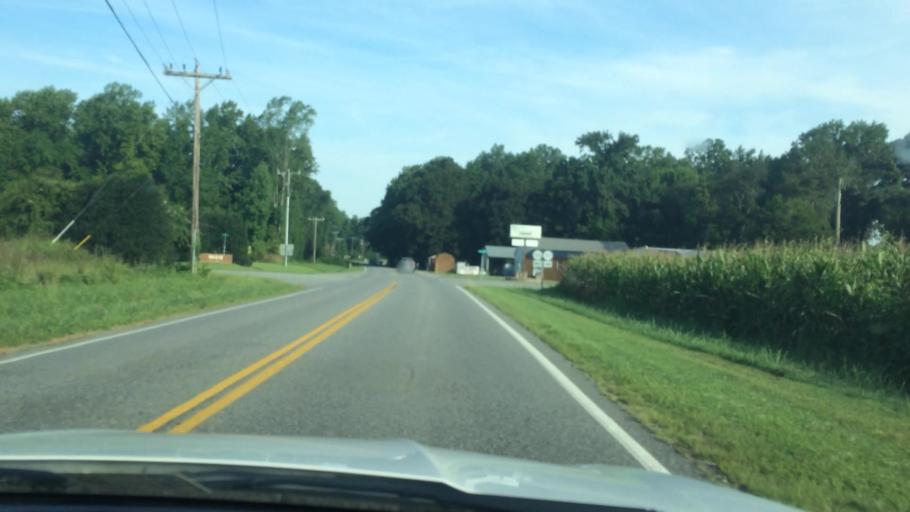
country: US
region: Virginia
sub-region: Middlesex County
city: Deltaville
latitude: 37.5021
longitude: -76.4155
